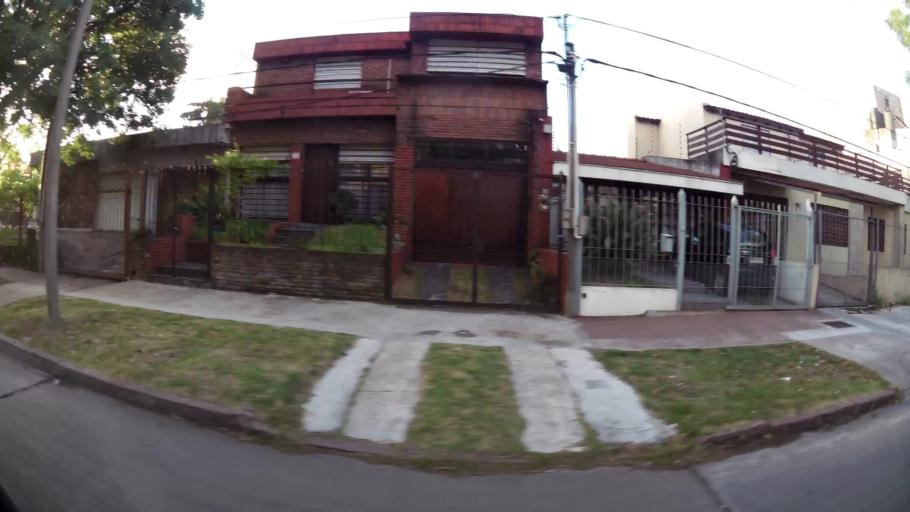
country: UY
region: Montevideo
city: Montevideo
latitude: -34.8803
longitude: -56.1518
